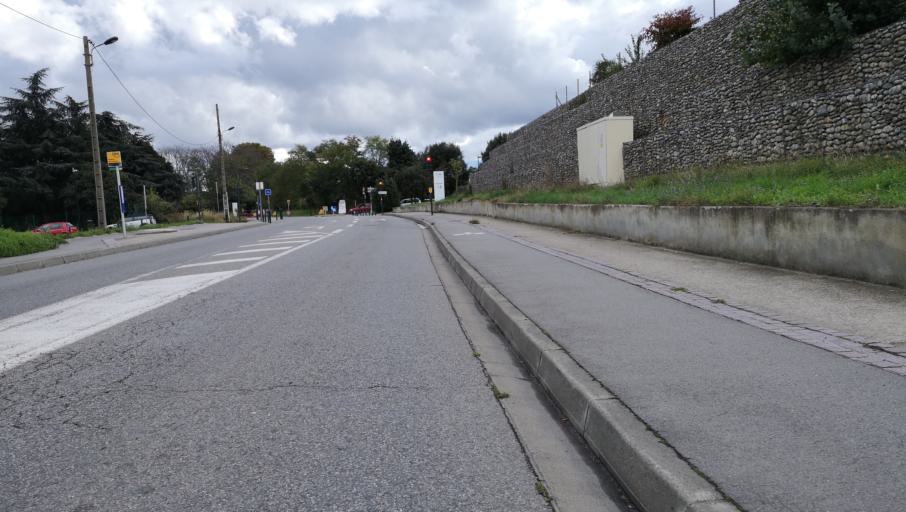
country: FR
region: Midi-Pyrenees
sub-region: Departement de la Haute-Garonne
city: Blagnac
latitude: 43.6117
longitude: 1.4031
